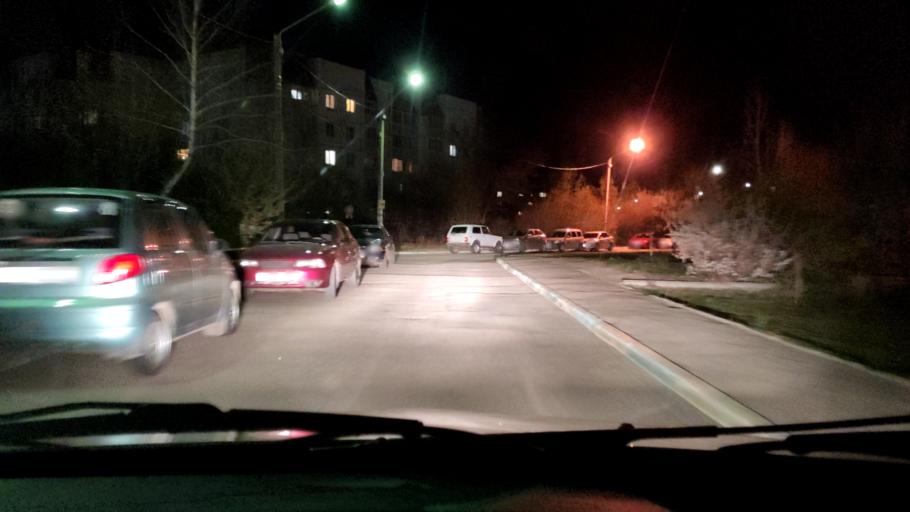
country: RU
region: Voronezj
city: Novaya Usman'
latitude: 51.6076
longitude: 39.3712
